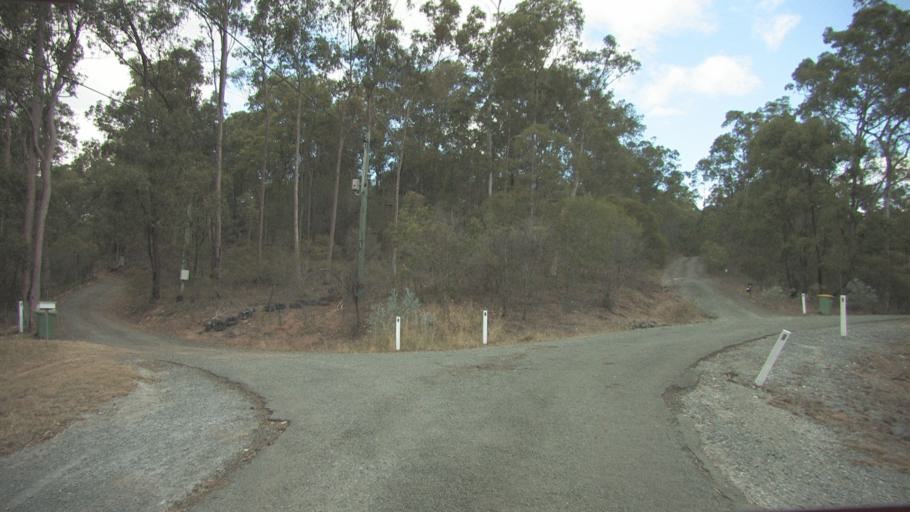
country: AU
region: Queensland
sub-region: Logan
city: Cedar Vale
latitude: -27.9345
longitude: 153.0523
